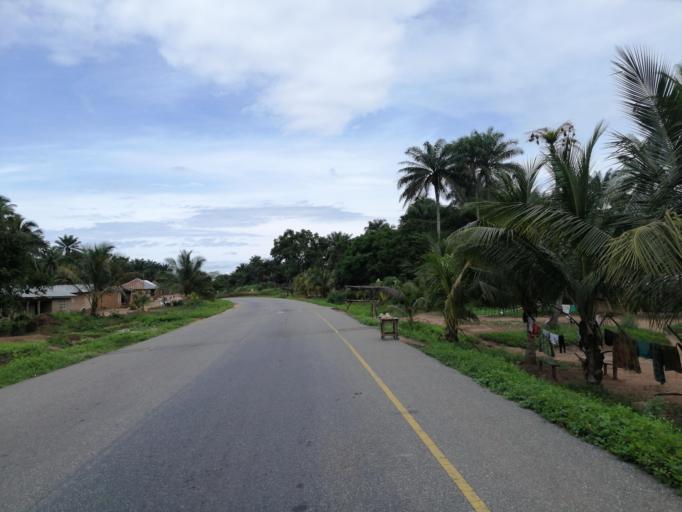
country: SL
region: Northern Province
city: Port Loko
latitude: 8.7630
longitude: -12.9083
